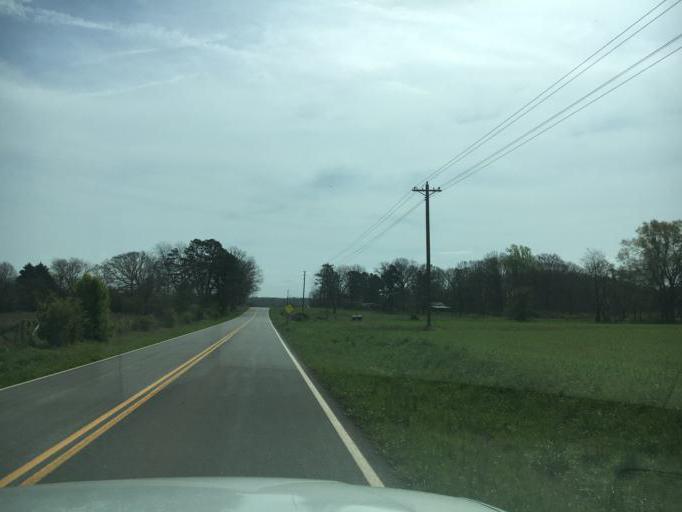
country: US
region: Georgia
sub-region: Franklin County
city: Lavonia
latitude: 34.3989
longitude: -83.0718
